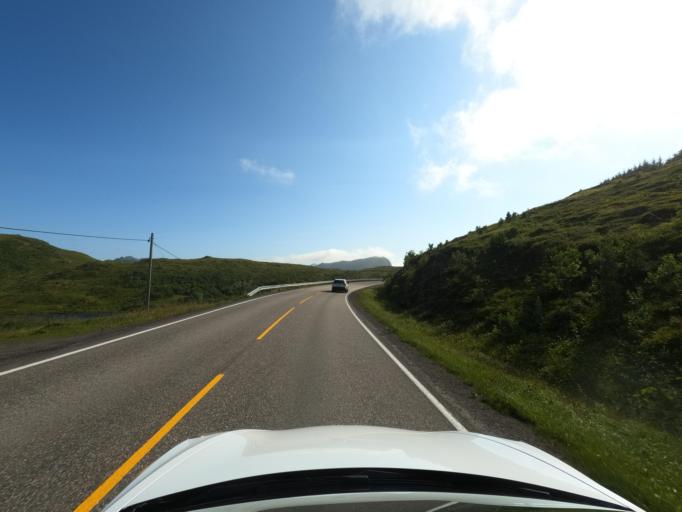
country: NO
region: Nordland
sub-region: Vestvagoy
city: Evjen
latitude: 68.2677
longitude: 13.8347
